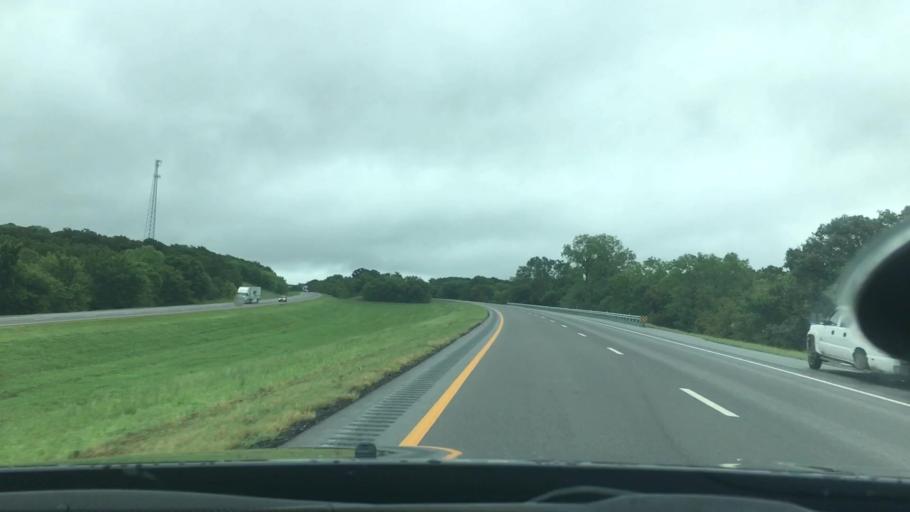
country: US
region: Oklahoma
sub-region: Okmulgee County
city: Henryetta
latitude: 35.4336
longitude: -95.8137
